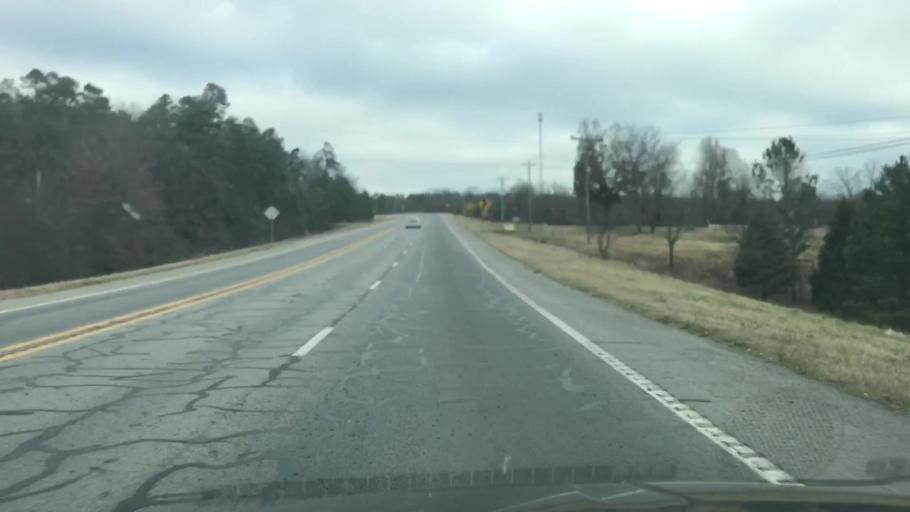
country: US
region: Arkansas
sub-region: Scott County
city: Waldron
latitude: 34.8153
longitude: -94.0389
